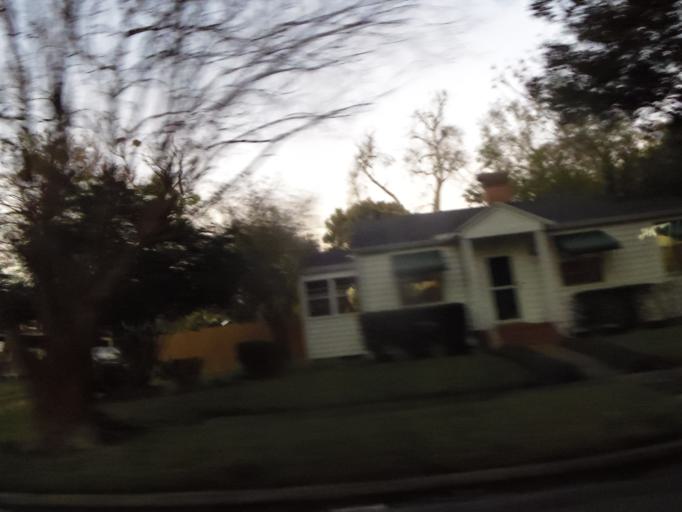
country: US
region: Florida
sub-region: Duval County
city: Jacksonville
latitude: 30.3031
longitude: -81.7112
